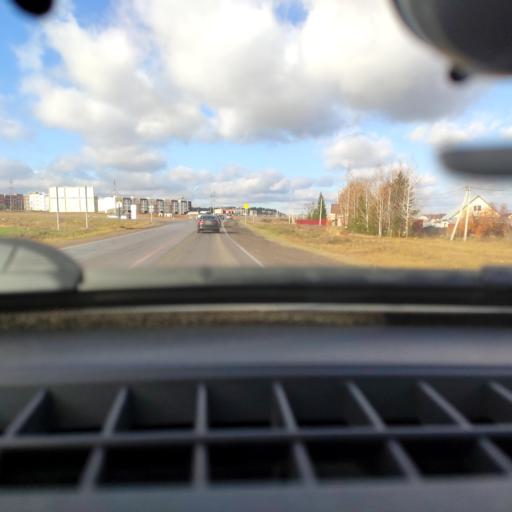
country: RU
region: Bashkortostan
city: Avdon
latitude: 54.7416
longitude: 55.7971
